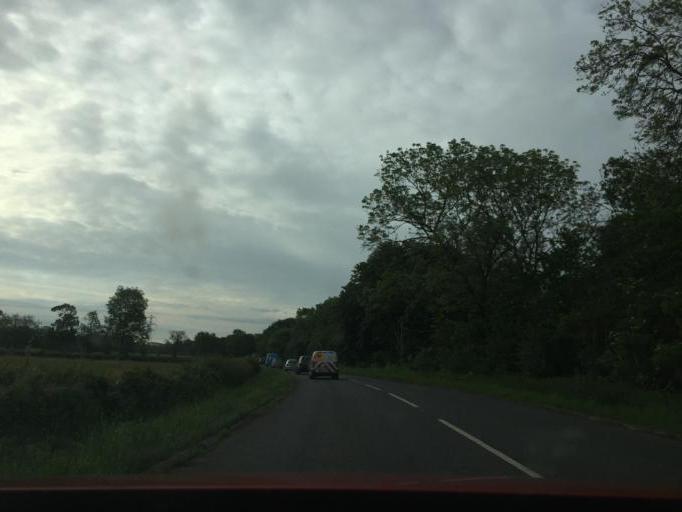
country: GB
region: England
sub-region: Leicestershire
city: Sapcote
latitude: 52.4620
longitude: -1.2954
